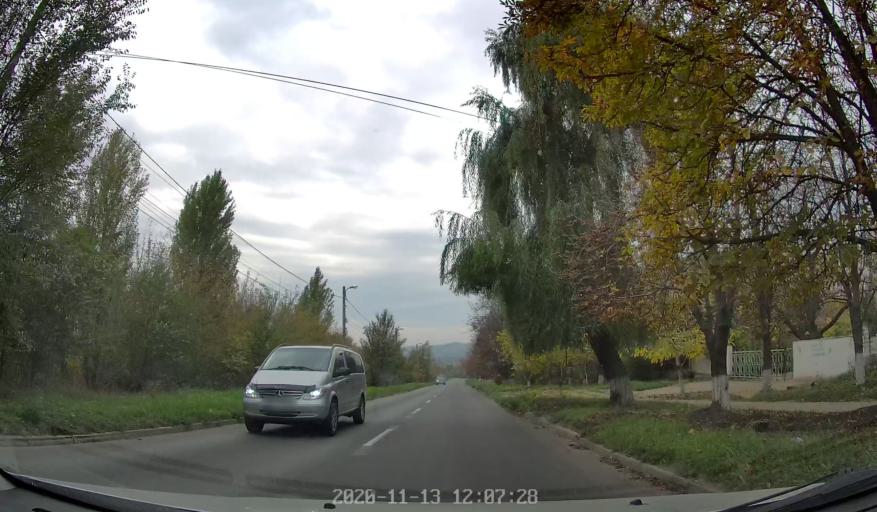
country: MD
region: Chisinau
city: Chisinau
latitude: 46.9741
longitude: 28.8350
